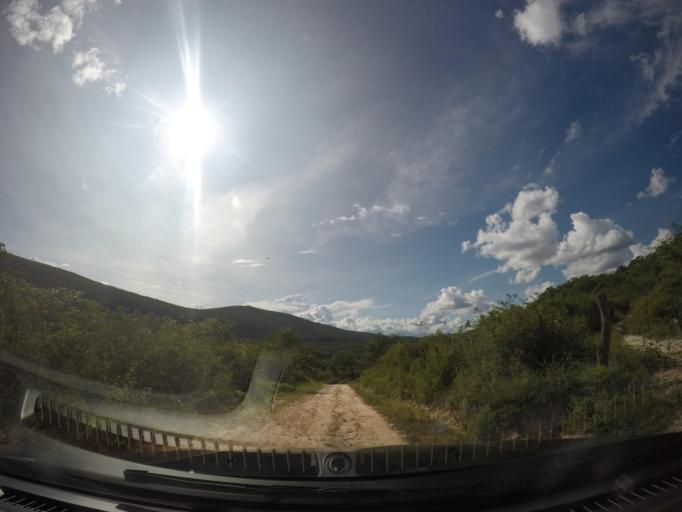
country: BR
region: Bahia
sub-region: Livramento Do Brumado
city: Livramento do Brumado
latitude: -13.2151
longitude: -41.6048
